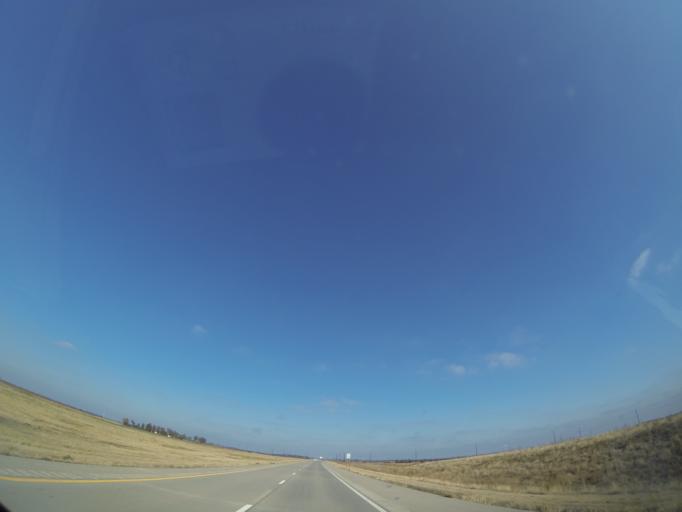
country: US
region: Kansas
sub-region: McPherson County
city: Inman
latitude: 38.1890
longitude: -97.8115
